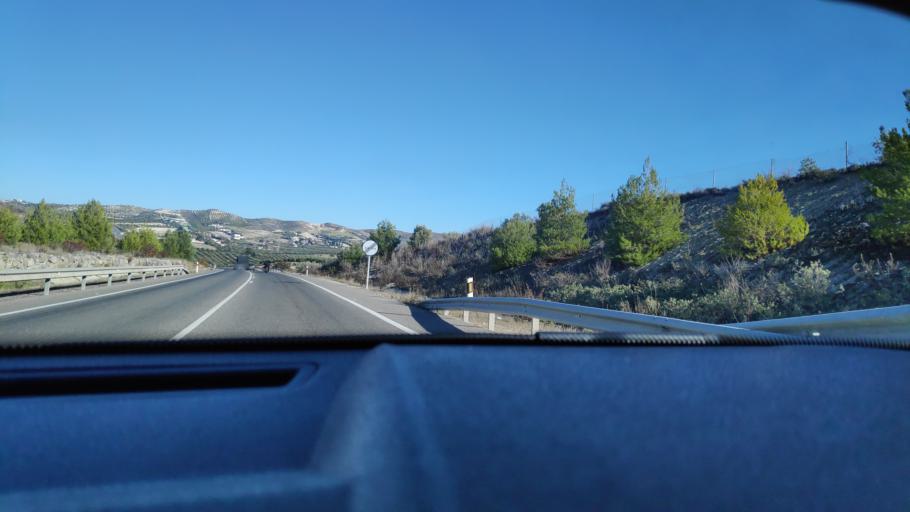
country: ES
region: Andalusia
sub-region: Province of Cordoba
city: Baena
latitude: 37.6087
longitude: -4.3014
